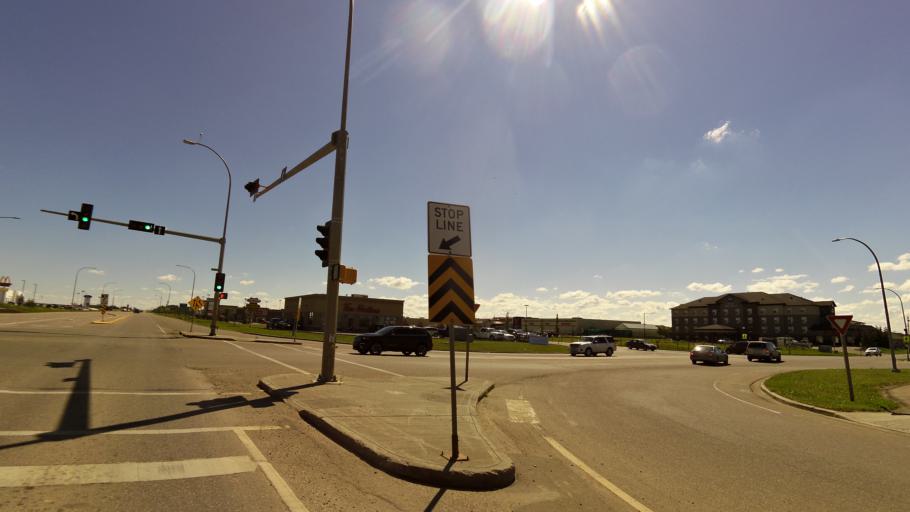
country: CA
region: Alberta
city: Wainwright
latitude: 52.8434
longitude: -110.8329
